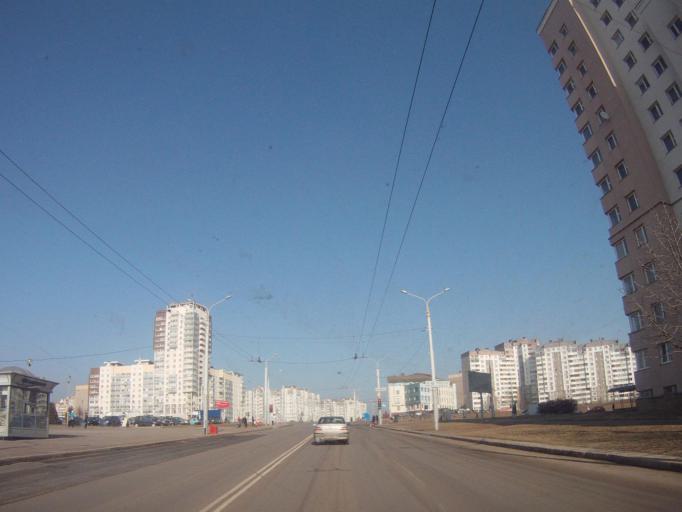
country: BY
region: Minsk
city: Novoye Medvezhino
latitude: 53.8871
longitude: 27.4293
